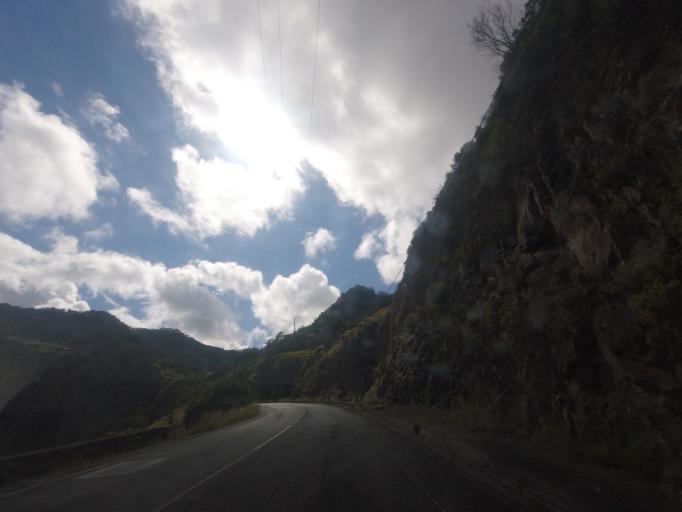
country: PT
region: Madeira
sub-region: Machico
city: Canical
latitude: 32.7384
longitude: -16.7530
